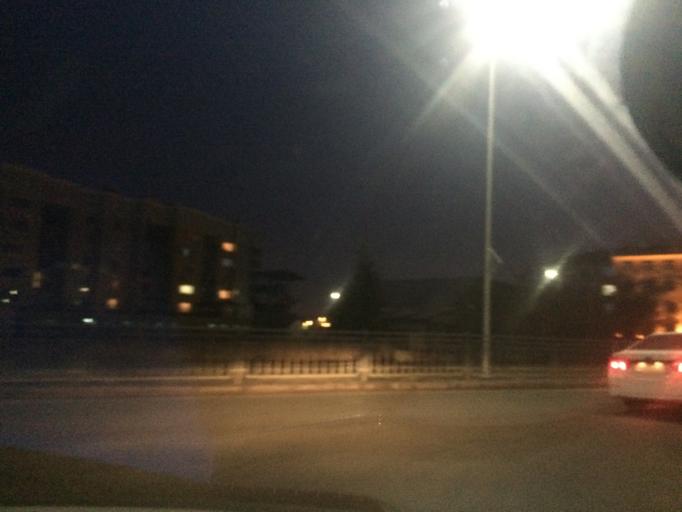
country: KZ
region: Astana Qalasy
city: Astana
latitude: 51.1414
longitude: 71.4148
